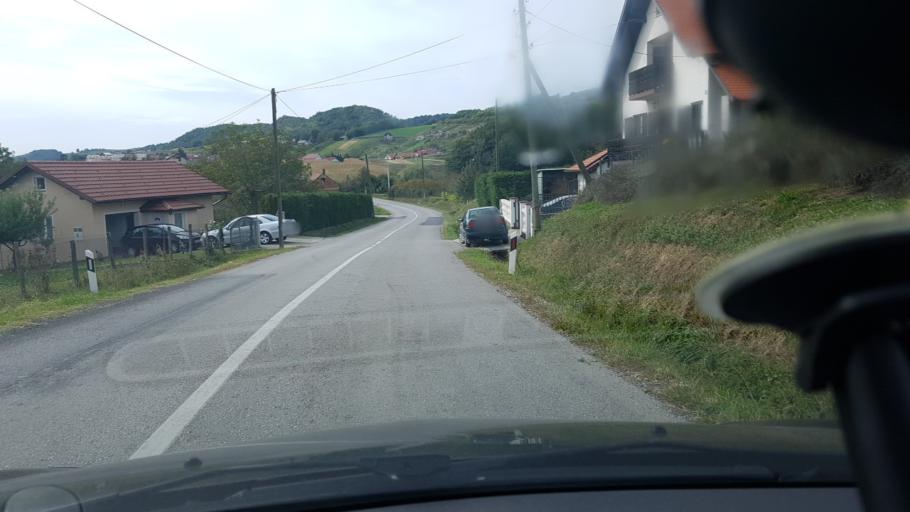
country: HR
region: Varazdinska
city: Ljubescica
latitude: 46.1058
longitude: 16.3714
